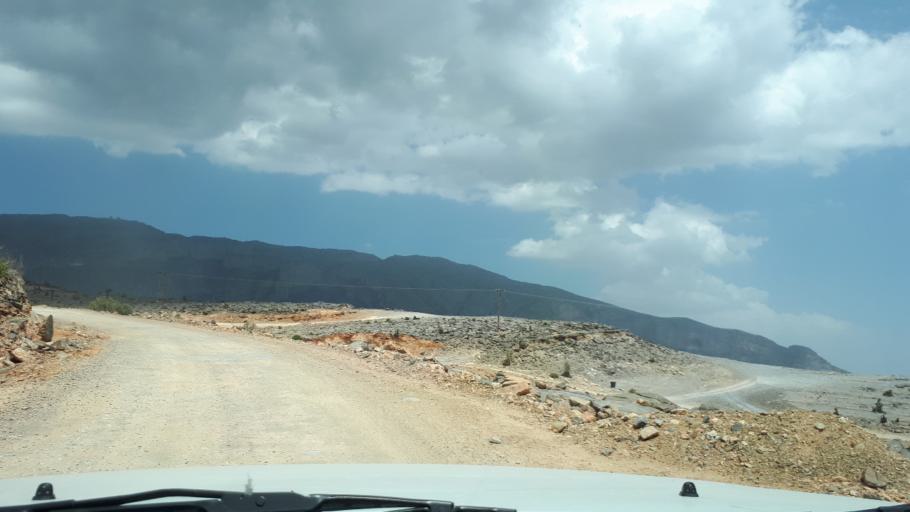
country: OM
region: Muhafazat ad Dakhiliyah
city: Bahla'
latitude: 23.2047
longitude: 57.2002
